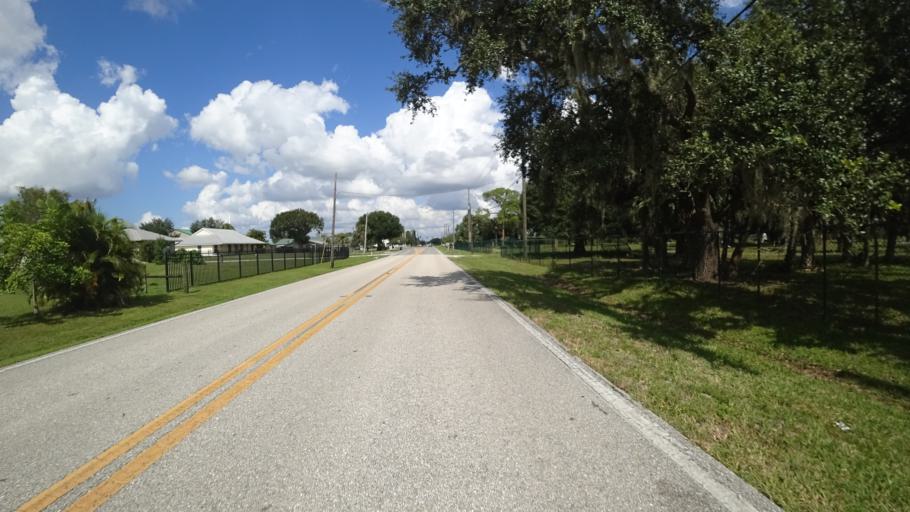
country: US
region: Florida
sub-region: Sarasota County
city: North Sarasota
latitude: 27.4159
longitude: -82.5177
